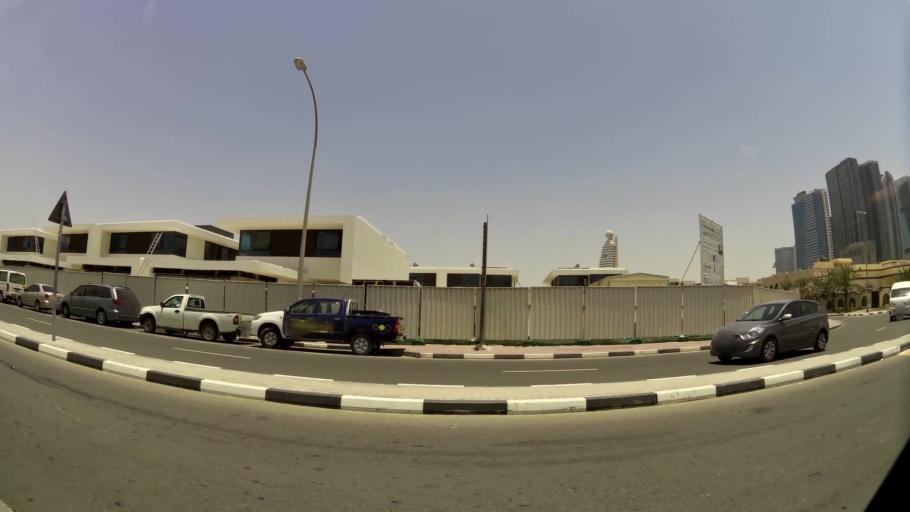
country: AE
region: Ash Shariqah
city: Sharjah
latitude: 25.2359
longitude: 55.2841
